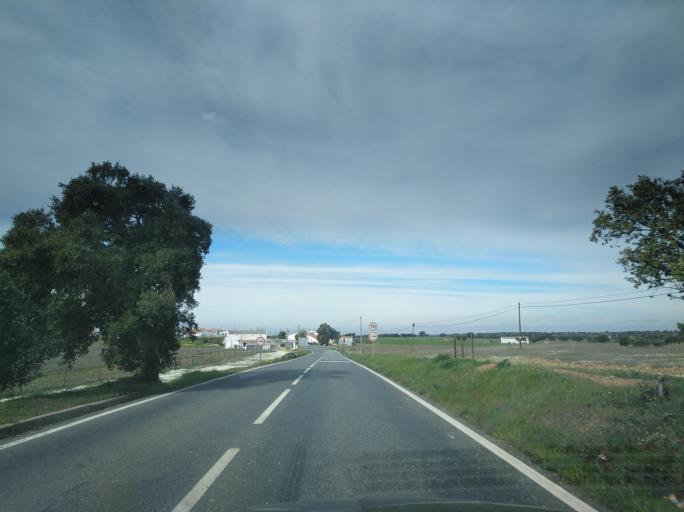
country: PT
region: Beja
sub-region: Mertola
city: Mertola
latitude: 37.7588
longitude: -7.8120
